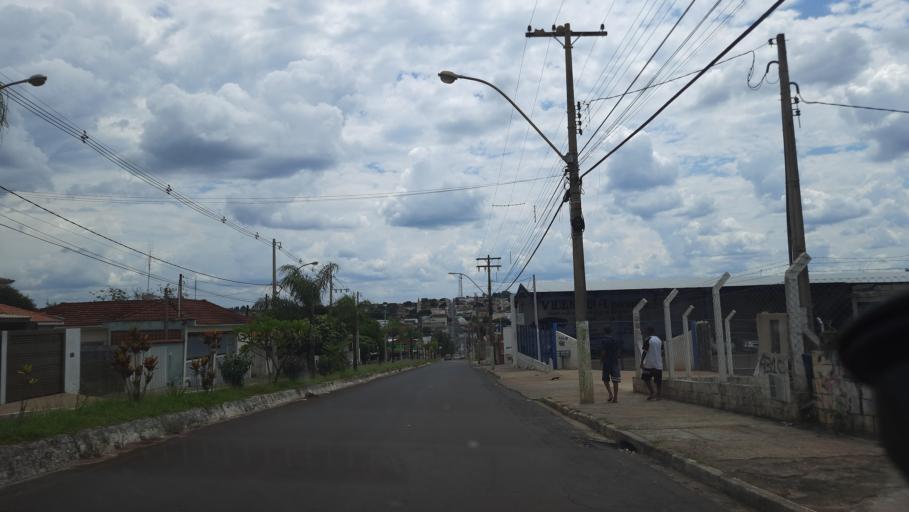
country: BR
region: Sao Paulo
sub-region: Cajuru
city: Cajuru
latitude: -21.2759
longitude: -47.2967
